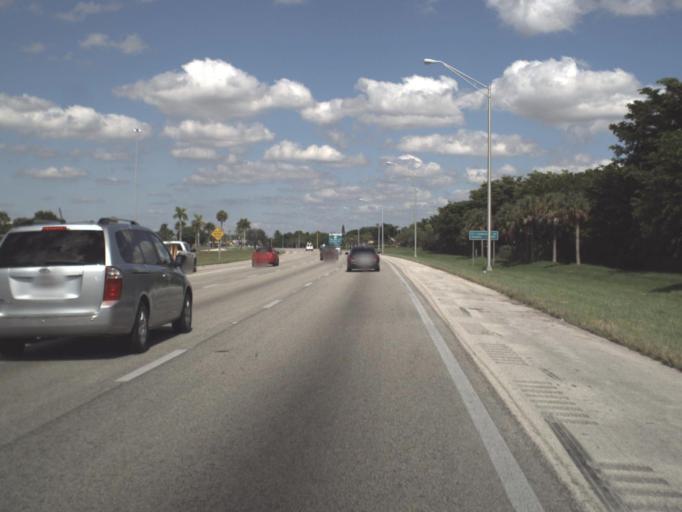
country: US
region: Florida
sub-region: Miami-Dade County
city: The Crossings
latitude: 25.6614
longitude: -80.3856
